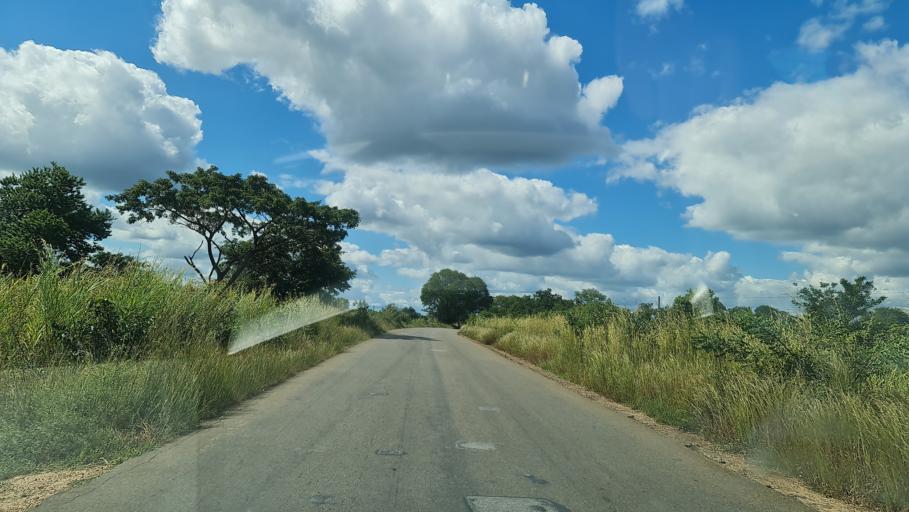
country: MZ
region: Zambezia
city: Quelimane
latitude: -17.5111
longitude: 36.2283
